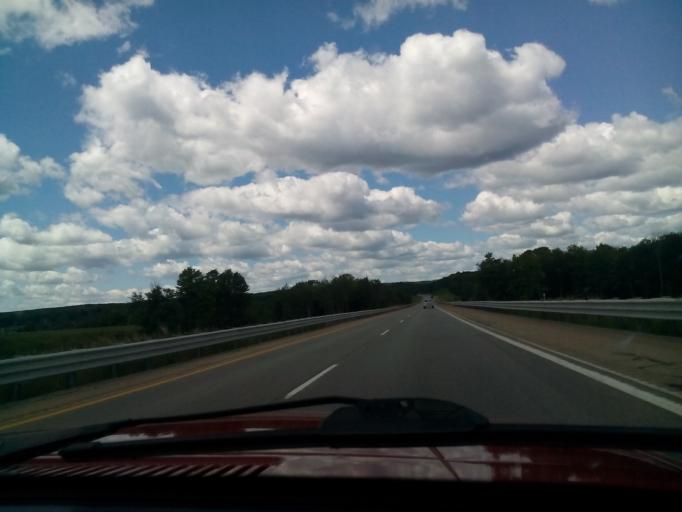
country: US
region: Michigan
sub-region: Ogemaw County
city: West Branch
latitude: 44.2751
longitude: -84.2800
